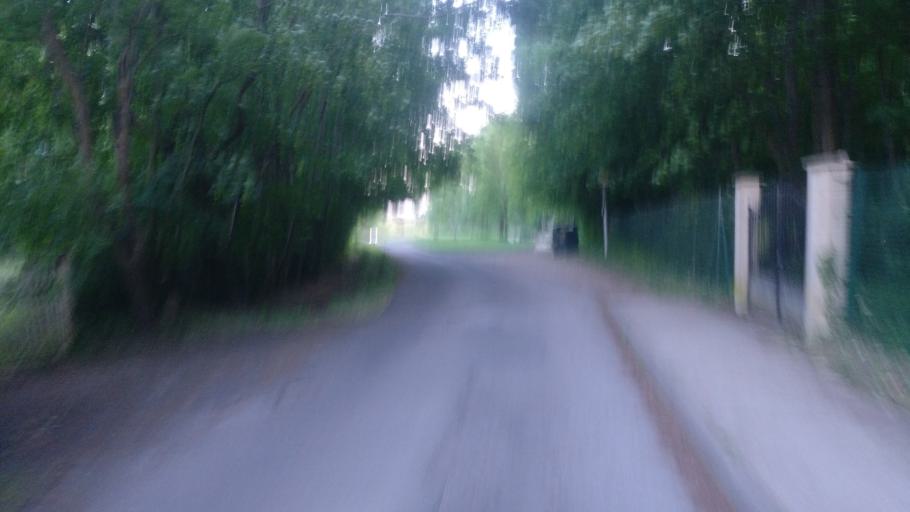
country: FR
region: Ile-de-France
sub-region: Departement du Val-de-Marne
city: Santeny
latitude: 48.7343
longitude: 2.5574
